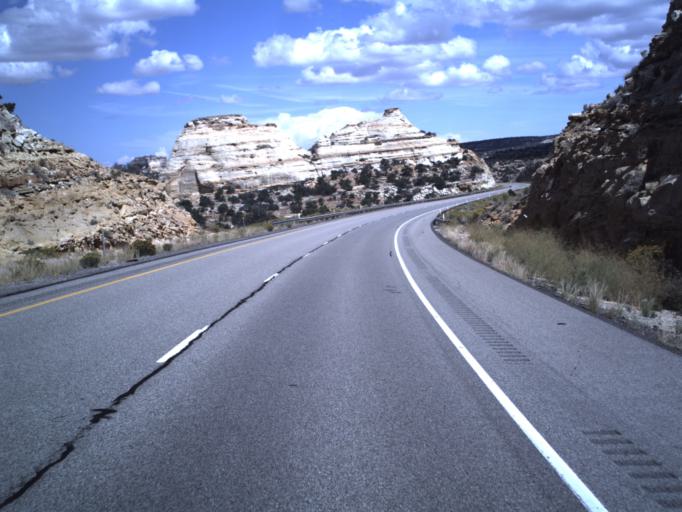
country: US
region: Utah
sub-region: Emery County
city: Ferron
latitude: 38.8514
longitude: -110.8817
